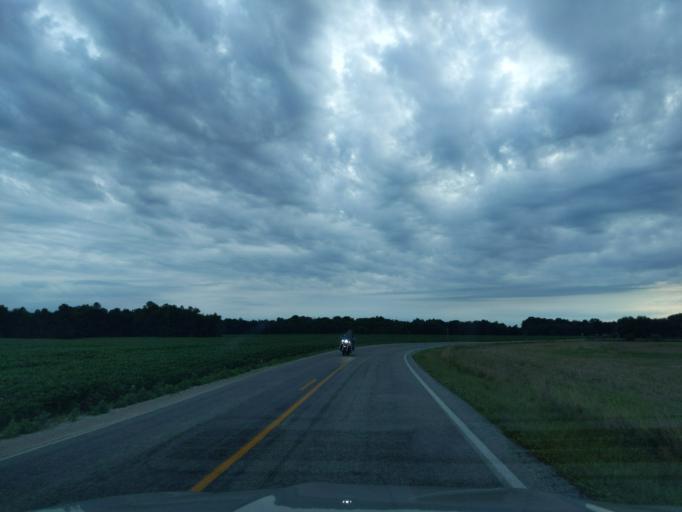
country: US
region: Indiana
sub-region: Ripley County
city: Sunman
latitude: 39.2021
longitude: -85.1729
